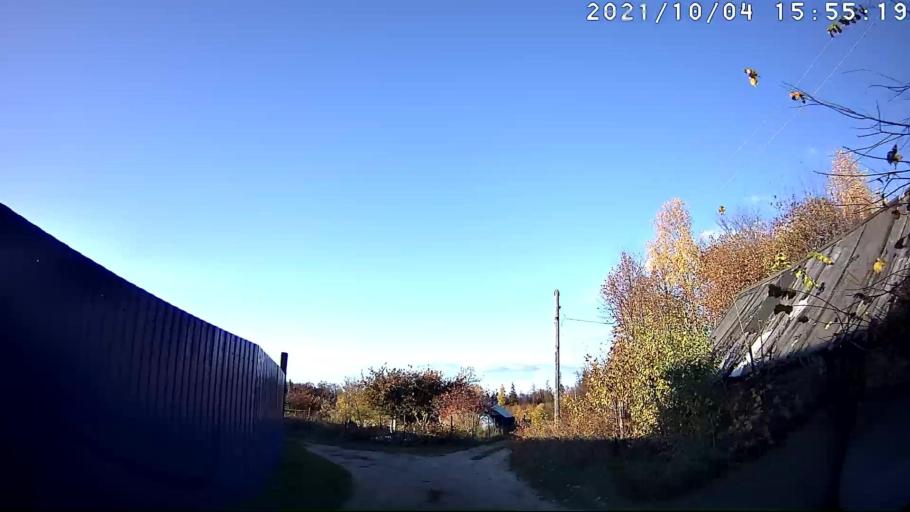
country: RU
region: Mariy-El
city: Sovetskiy
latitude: 56.5466
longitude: 48.4114
